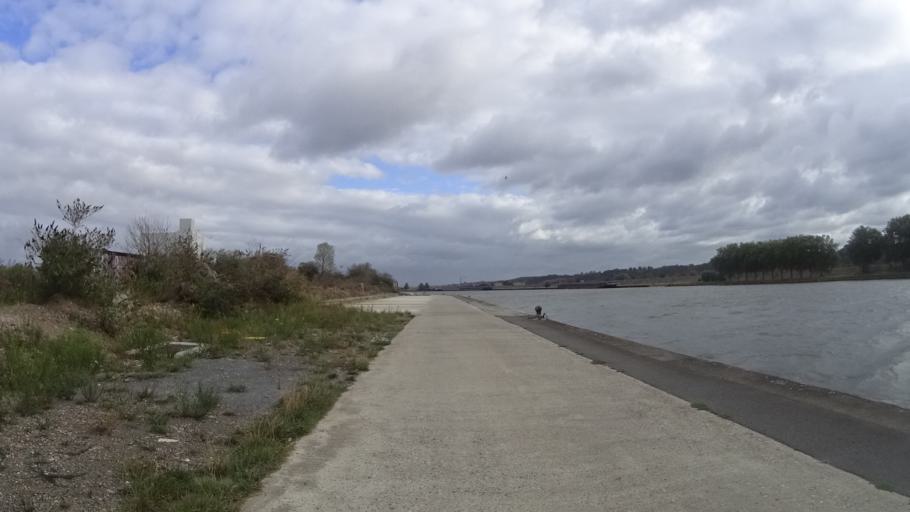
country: BE
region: Wallonia
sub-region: Province de Liege
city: Oupeye
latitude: 50.7067
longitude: 5.6669
